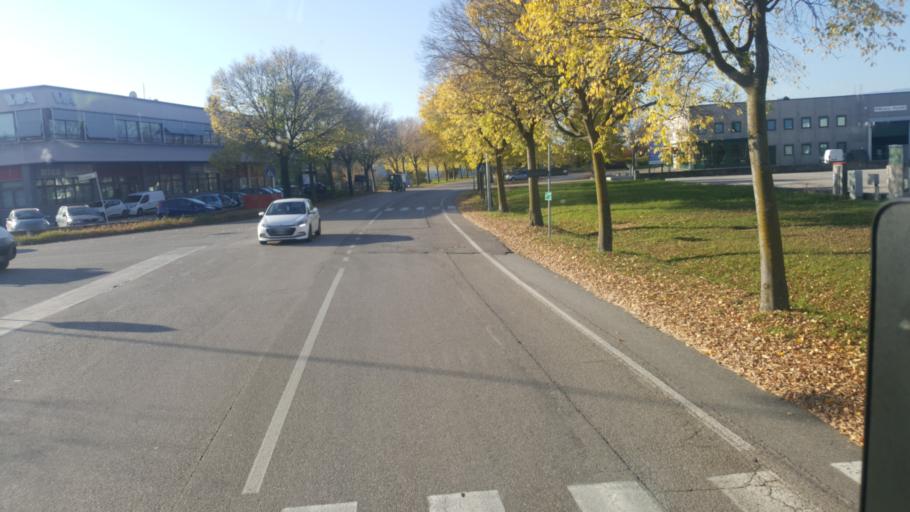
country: IT
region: Friuli Venezia Giulia
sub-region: Provincia di Pordenone
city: Azzano Decimo
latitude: 45.9324
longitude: 12.6562
